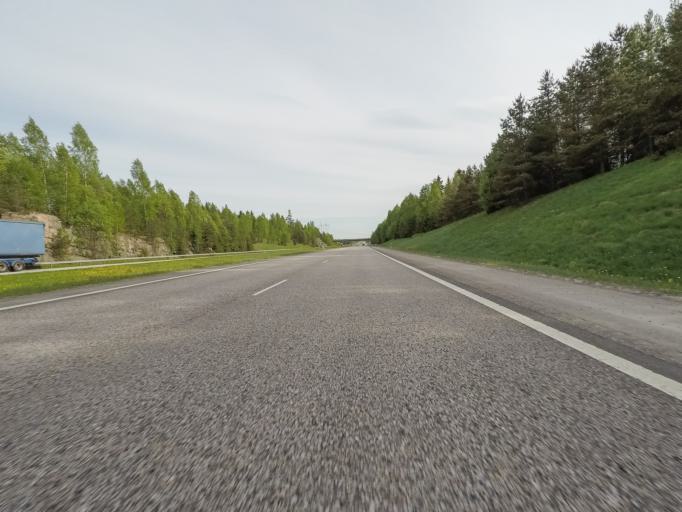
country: FI
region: Uusimaa
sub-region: Helsinki
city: Nurmijaervi
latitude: 60.5466
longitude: 24.8373
